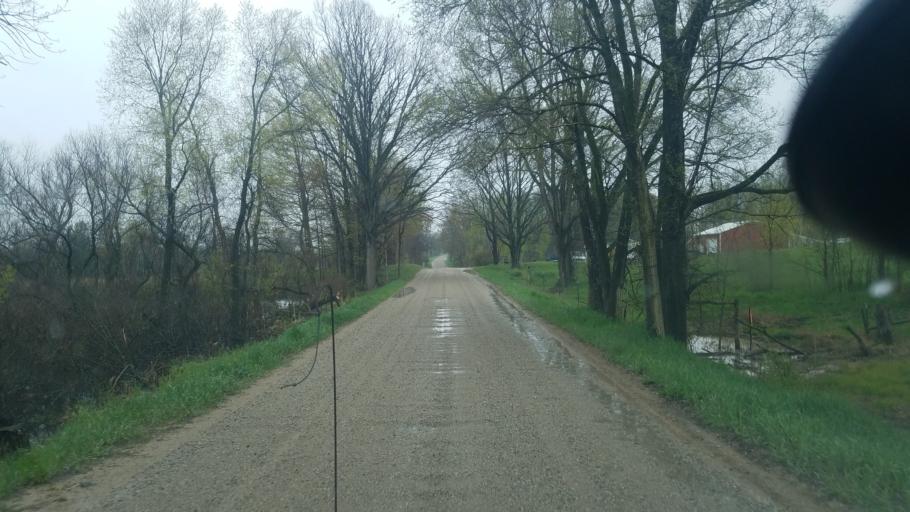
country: US
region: Michigan
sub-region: Montcalm County
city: Lakeview
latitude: 43.4699
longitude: -85.3332
